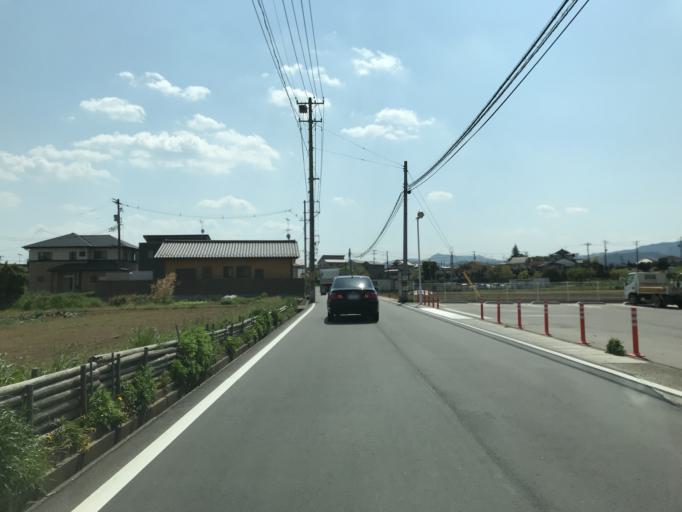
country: JP
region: Ibaraki
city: Kitaibaraki
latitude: 36.8956
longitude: 140.7557
